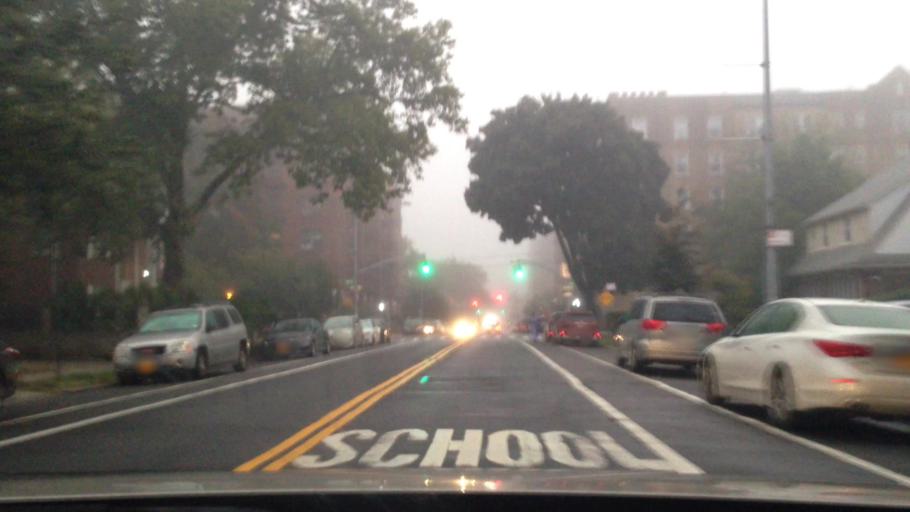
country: US
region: New York
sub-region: Kings County
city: Brooklyn
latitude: 40.6147
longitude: -73.9495
